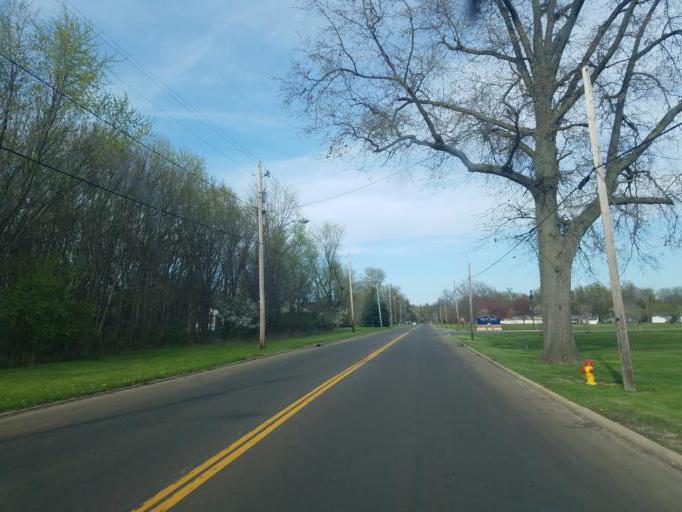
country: US
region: Ohio
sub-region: Ashtabula County
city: Ashtabula
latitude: 41.8901
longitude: -80.8343
